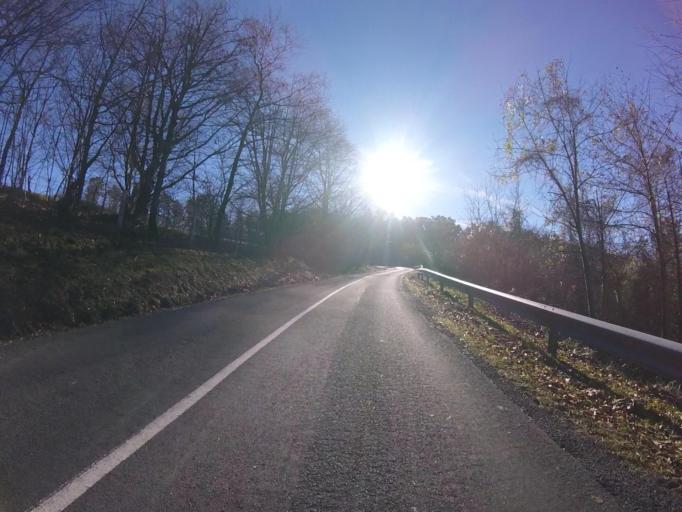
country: ES
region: Basque Country
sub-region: Provincia de Guipuzcoa
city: Irun
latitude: 43.3131
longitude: -1.7581
